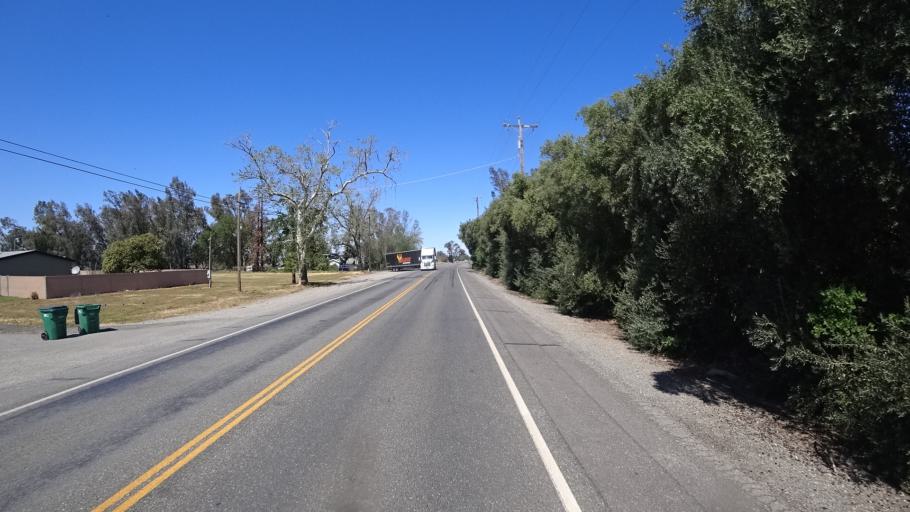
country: US
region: California
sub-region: Glenn County
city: Orland
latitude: 39.7829
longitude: -122.1976
